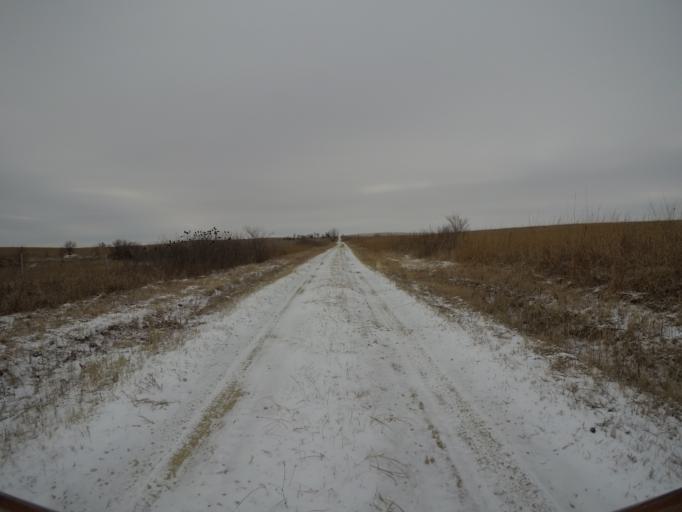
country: US
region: Kansas
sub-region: Wabaunsee County
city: Alma
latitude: 38.9004
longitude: -96.1136
